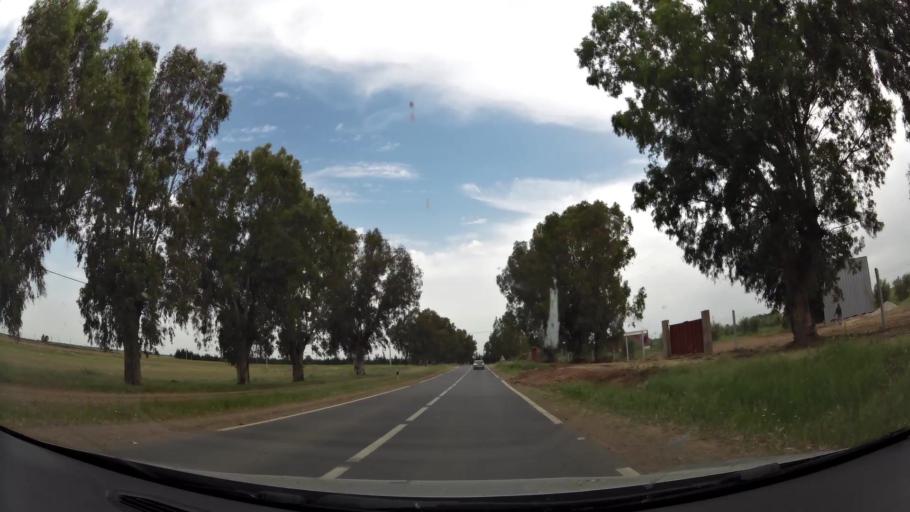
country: MA
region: Rabat-Sale-Zemmour-Zaer
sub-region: Khemisset
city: Tiflet
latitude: 33.8641
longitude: -6.2726
